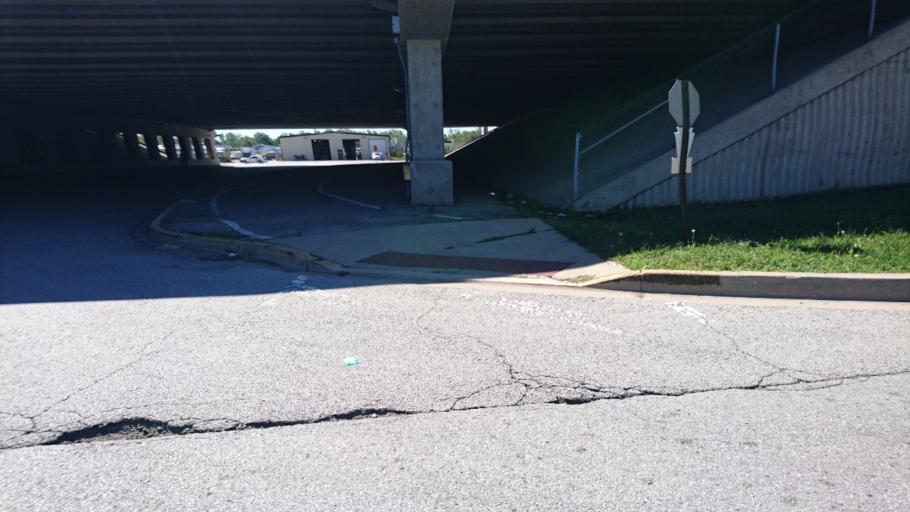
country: US
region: Illinois
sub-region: Cook County
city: Lansing
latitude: 41.5783
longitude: -87.5485
